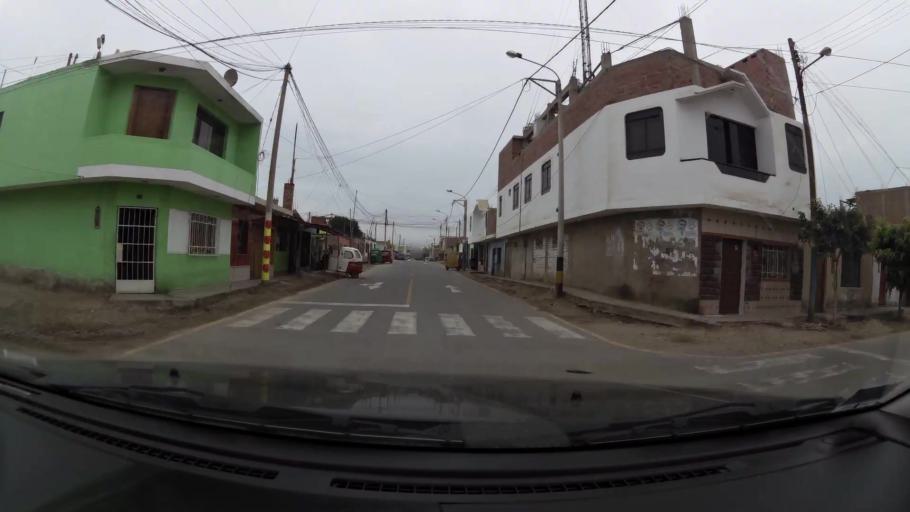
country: PE
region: Ica
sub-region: Provincia de Pisco
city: Pisco
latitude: -13.7151
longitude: -76.1984
